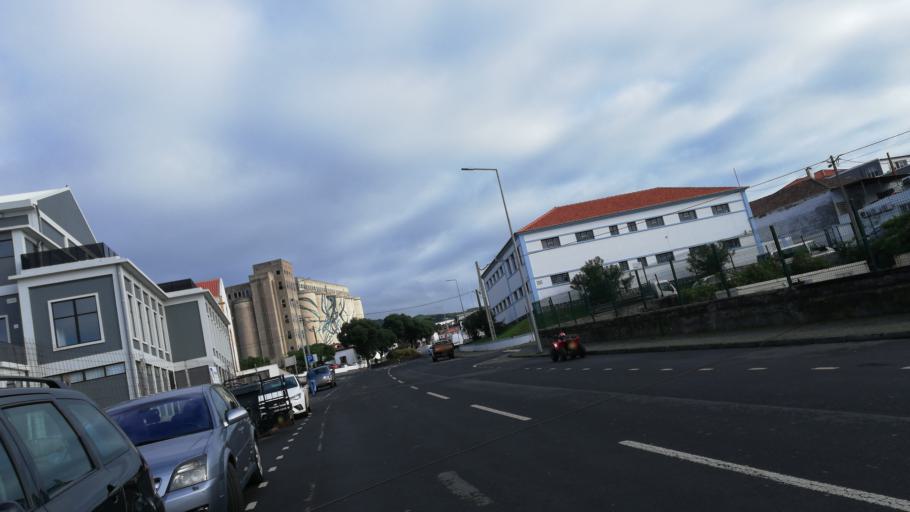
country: PT
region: Azores
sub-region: Angra do Heroismo
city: Angra do Heroismo
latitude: 38.6533
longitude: -27.2133
